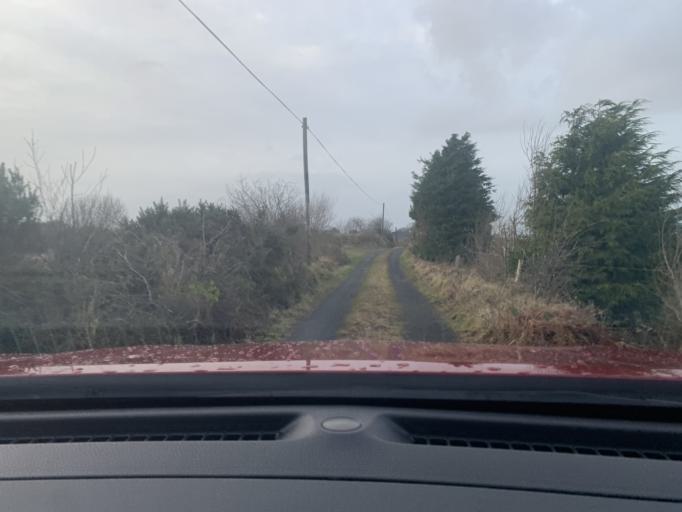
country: IE
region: Connaught
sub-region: Roscommon
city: Ballaghaderreen
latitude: 53.9545
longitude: -8.5408
